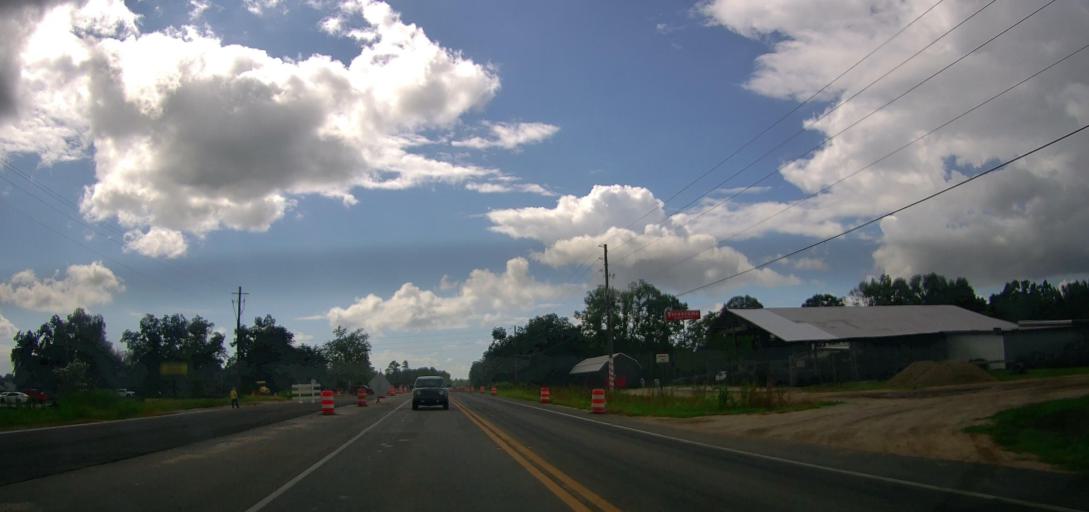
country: US
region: Georgia
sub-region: Coffee County
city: Douglas
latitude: 31.5210
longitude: -82.8921
